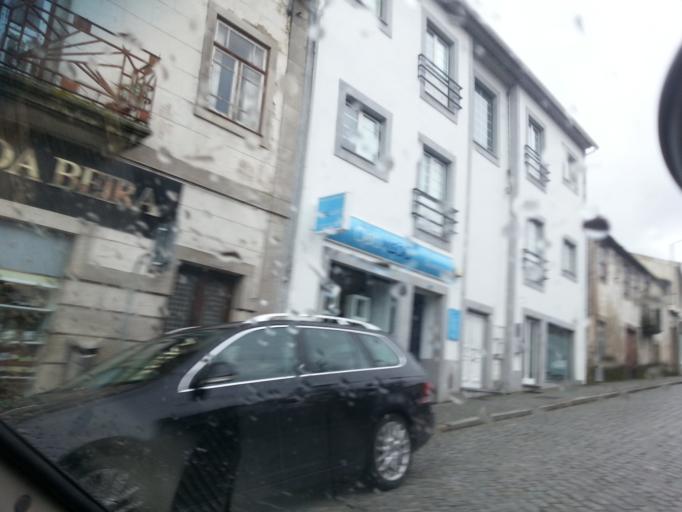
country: PT
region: Guarda
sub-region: Celorico da Beira
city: Celorico da Beira
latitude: 40.6372
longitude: -7.3907
